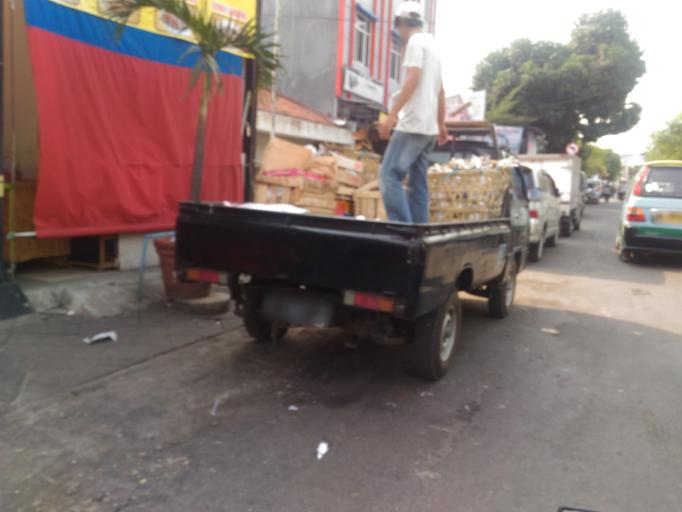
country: ID
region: Banten
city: Tangerang
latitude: -6.1757
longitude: 106.6320
